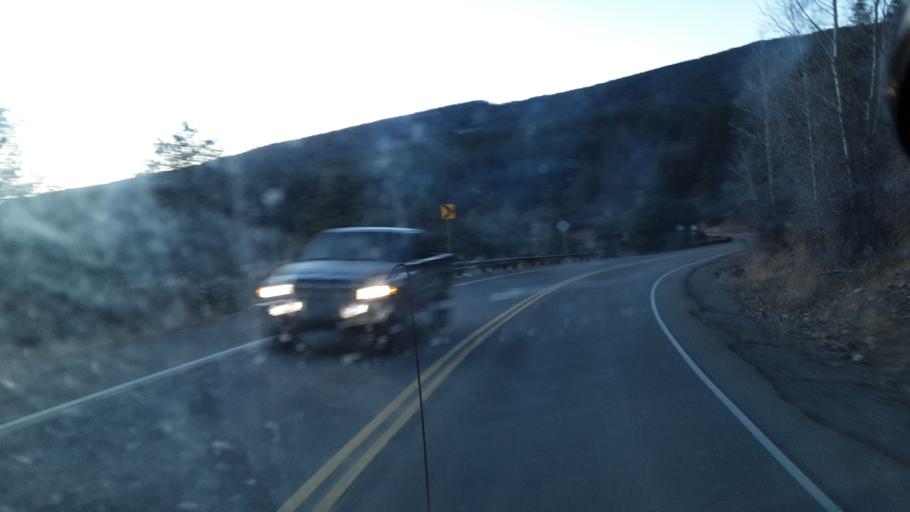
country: US
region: Colorado
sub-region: La Plata County
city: Durango
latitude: 37.3311
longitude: -107.7368
